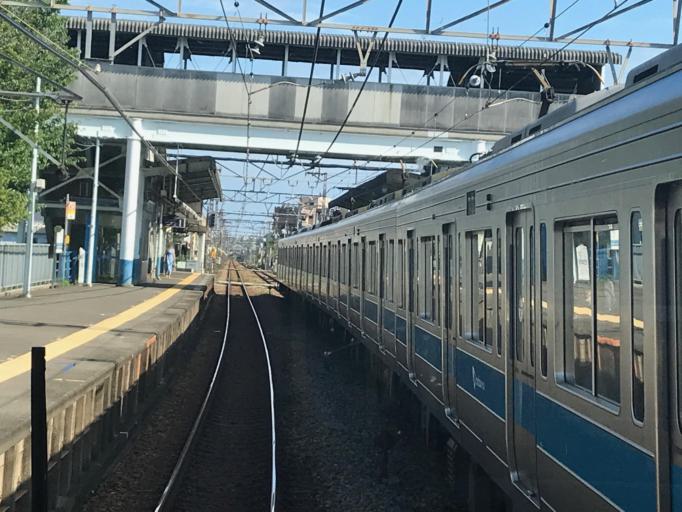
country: JP
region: Kanagawa
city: Odawara
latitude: 35.3031
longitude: 139.1438
